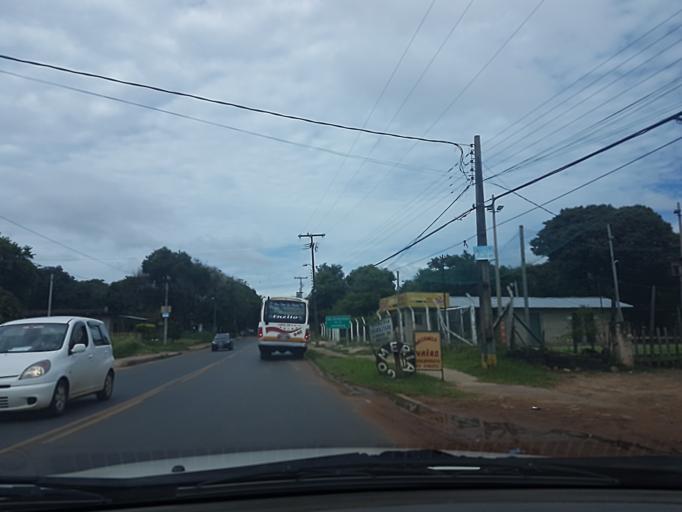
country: PY
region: Central
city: San Lorenzo
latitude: -25.2597
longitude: -57.4772
